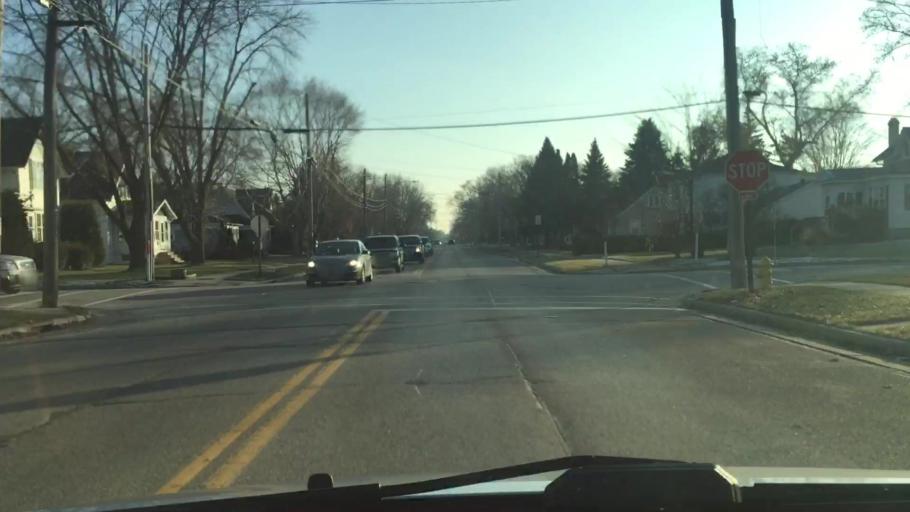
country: US
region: Wisconsin
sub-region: Waukesha County
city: Oconomowoc
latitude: 43.1026
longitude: -88.4959
